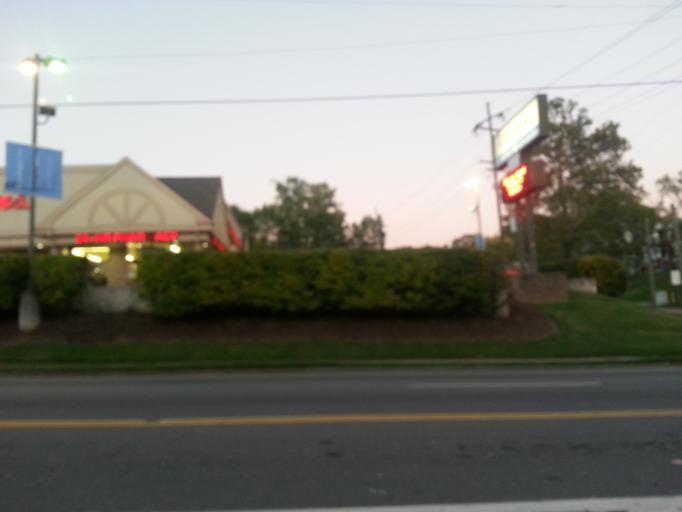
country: US
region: Tennessee
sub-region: Knox County
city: Knoxville
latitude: 35.9946
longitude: -83.9212
